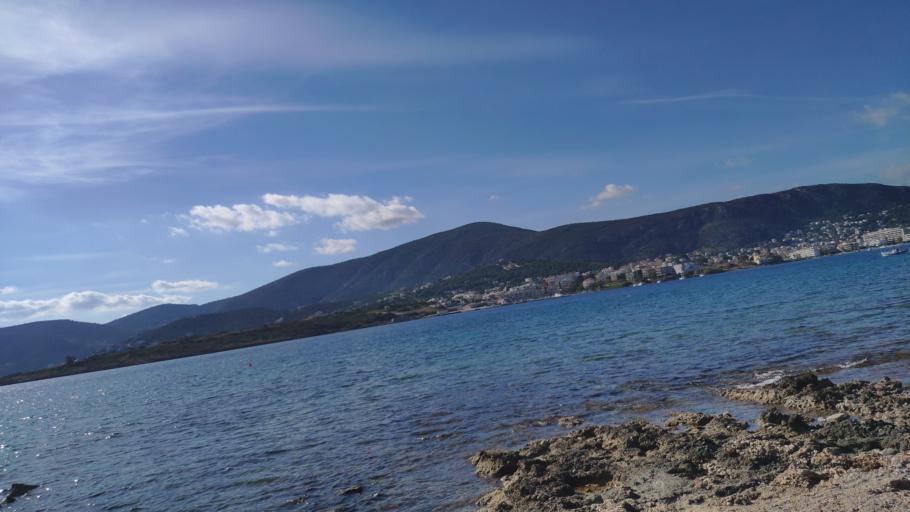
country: GR
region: Attica
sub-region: Nomarchia Anatolikis Attikis
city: Limin Mesoyaias
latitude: 37.8916
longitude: 24.0209
